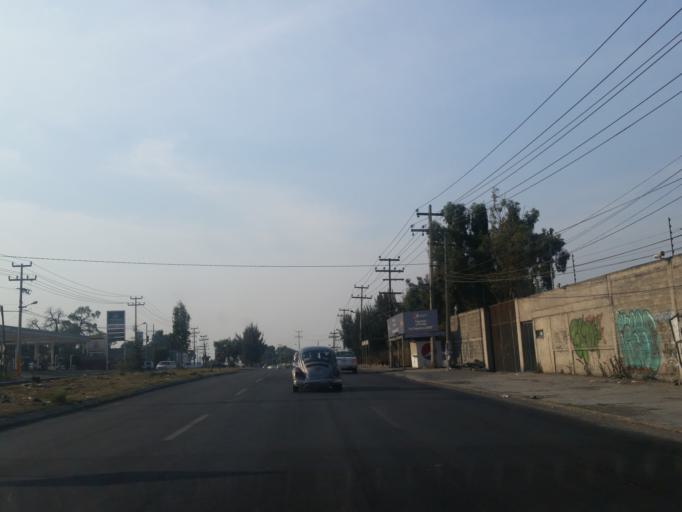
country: MX
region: Mexico
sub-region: La Paz
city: Emiliano Zapata
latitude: 19.3472
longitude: -98.9642
